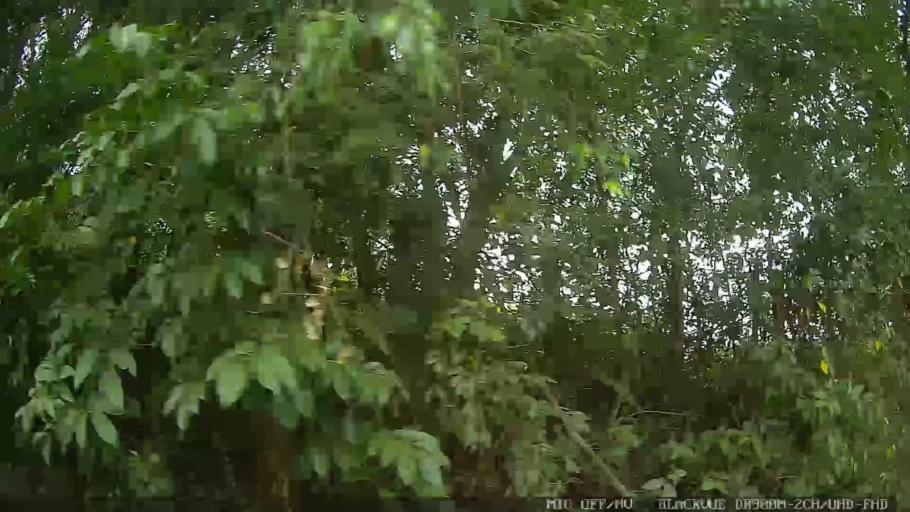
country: BR
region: Sao Paulo
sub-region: Atibaia
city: Atibaia
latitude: -23.1481
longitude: -46.5706
